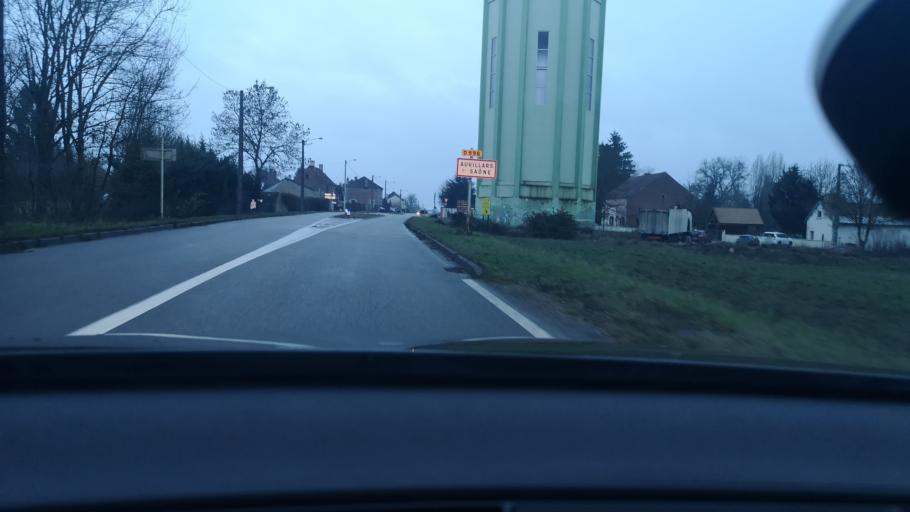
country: FR
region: Bourgogne
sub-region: Departement de la Cote-d'Or
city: Seurre
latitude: 47.0675
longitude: 5.0983
